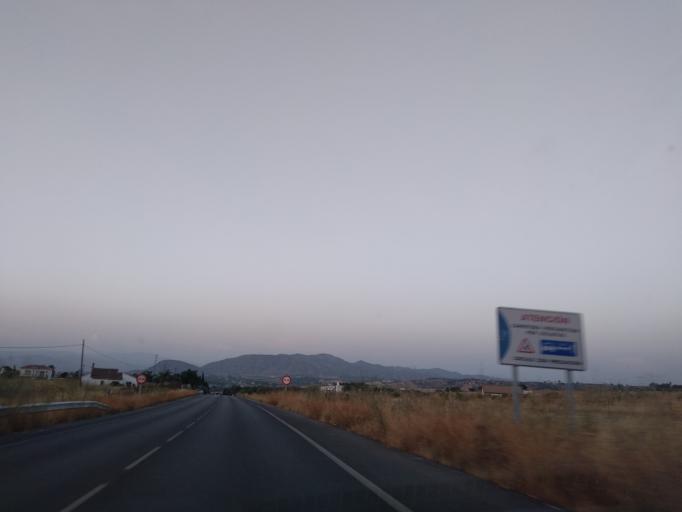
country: ES
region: Andalusia
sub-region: Provincia de Malaga
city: Alhaurin el Grande
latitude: 36.6578
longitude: -4.6743
